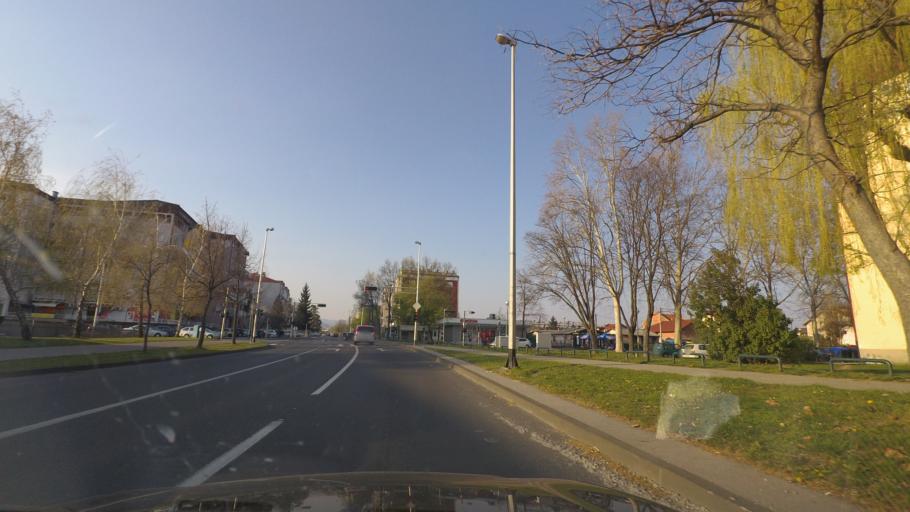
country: HR
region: Grad Zagreb
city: Dubrava
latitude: 45.8224
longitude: 16.0641
